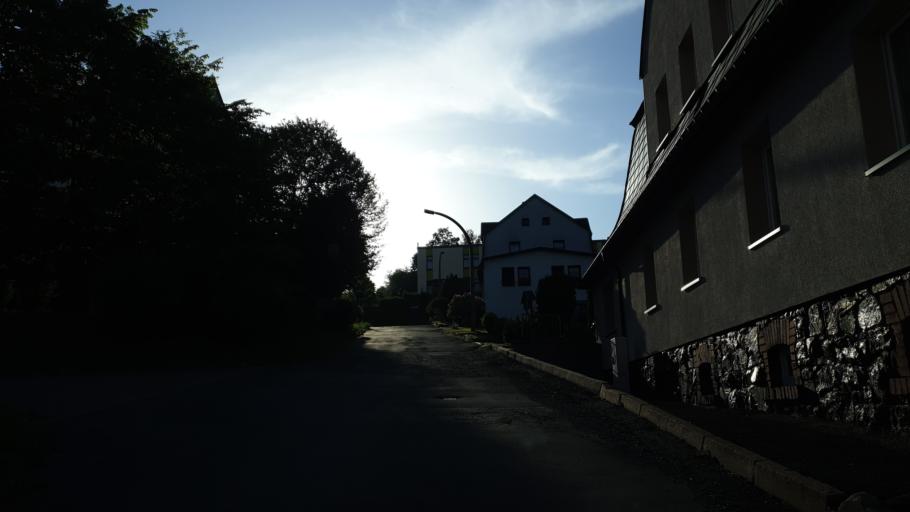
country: DE
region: Saxony
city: Klingenthal
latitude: 50.3611
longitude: 12.4575
